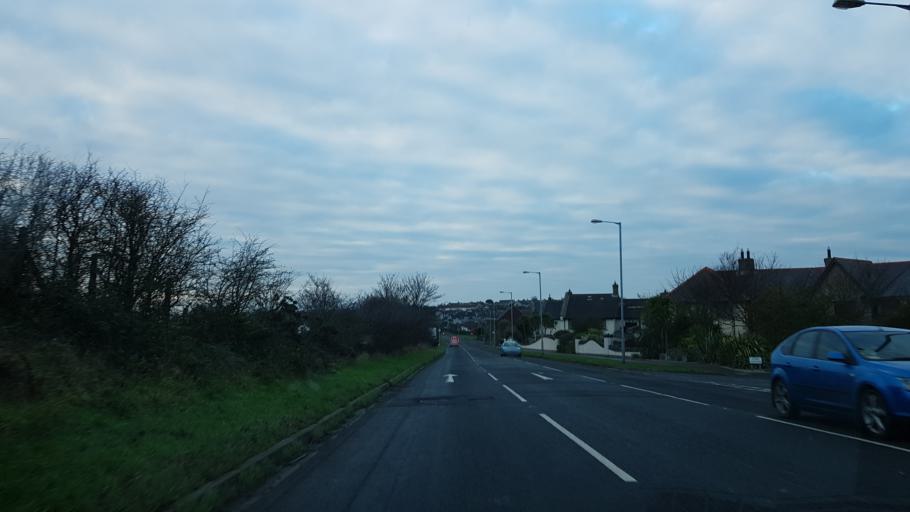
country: GB
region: Northern Ireland
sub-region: North Down District
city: Bangor
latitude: 54.6729
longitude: -5.6096
